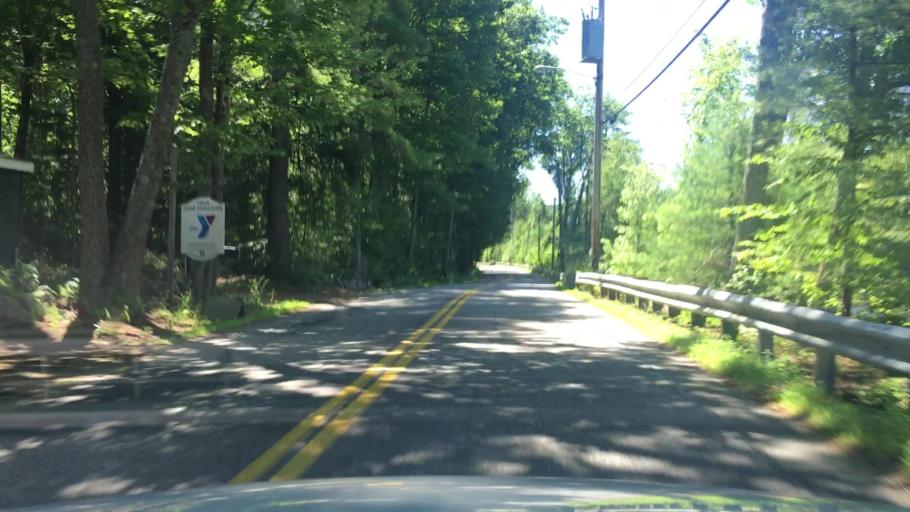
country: US
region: New Hampshire
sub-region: Merrimack County
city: Boscawen
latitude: 43.2553
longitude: -71.6212
